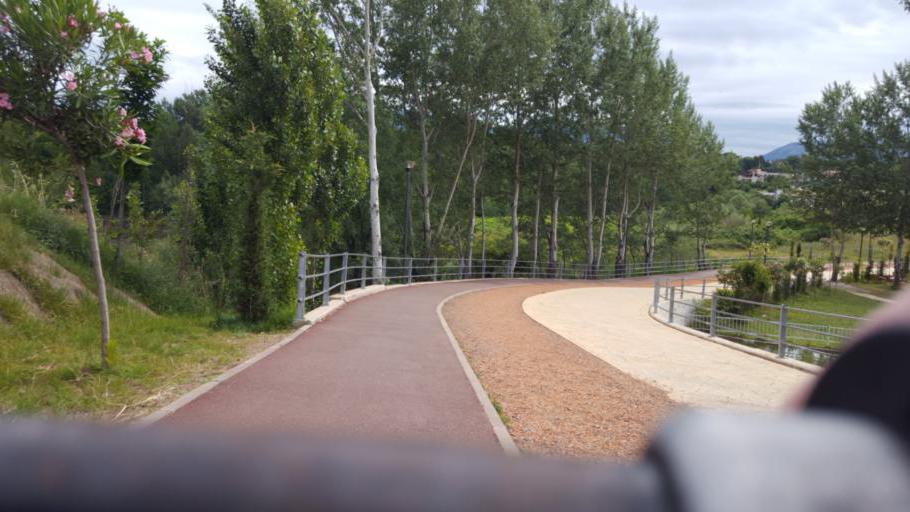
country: AL
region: Tirane
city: Tirana
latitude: 41.3061
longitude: 19.8222
